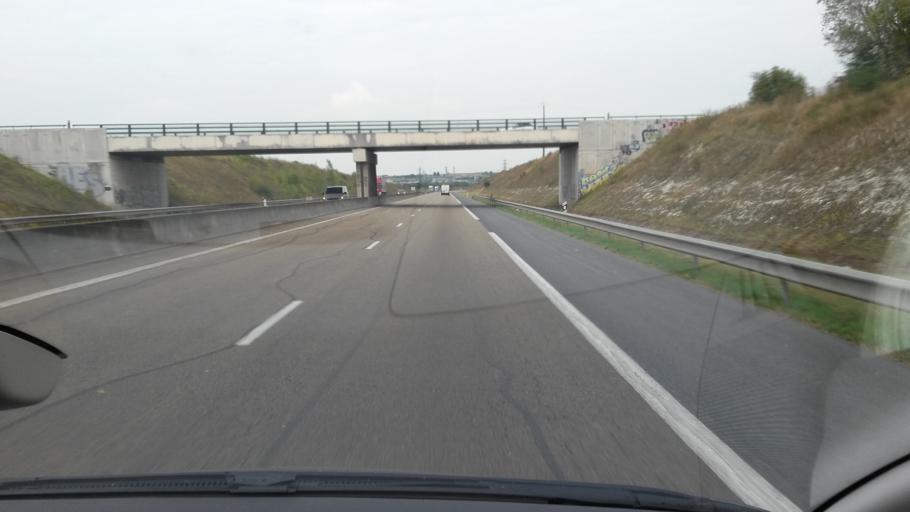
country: FR
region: Champagne-Ardenne
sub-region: Departement de la Marne
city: Cernay-les-Reims
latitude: 49.2593
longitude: 4.0856
